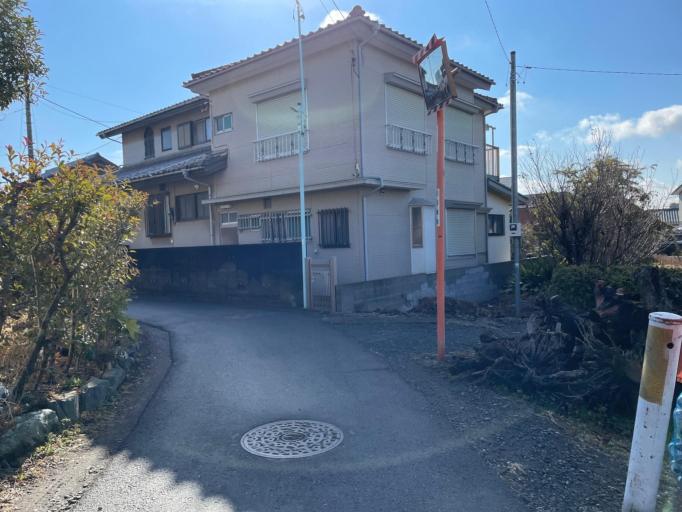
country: JP
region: Tokyo
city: Kokubunji
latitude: 35.6762
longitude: 139.4640
